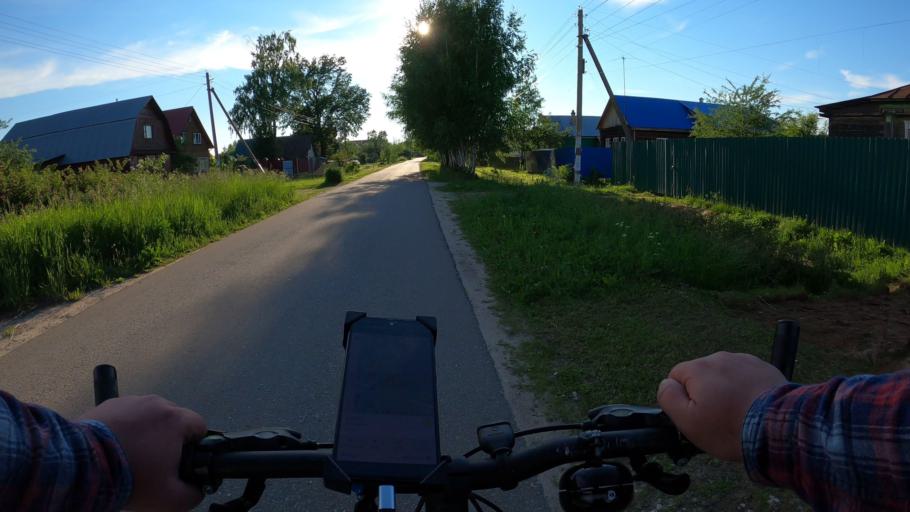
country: RU
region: Moskovskaya
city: Ashitkovo
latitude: 55.4555
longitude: 38.5845
